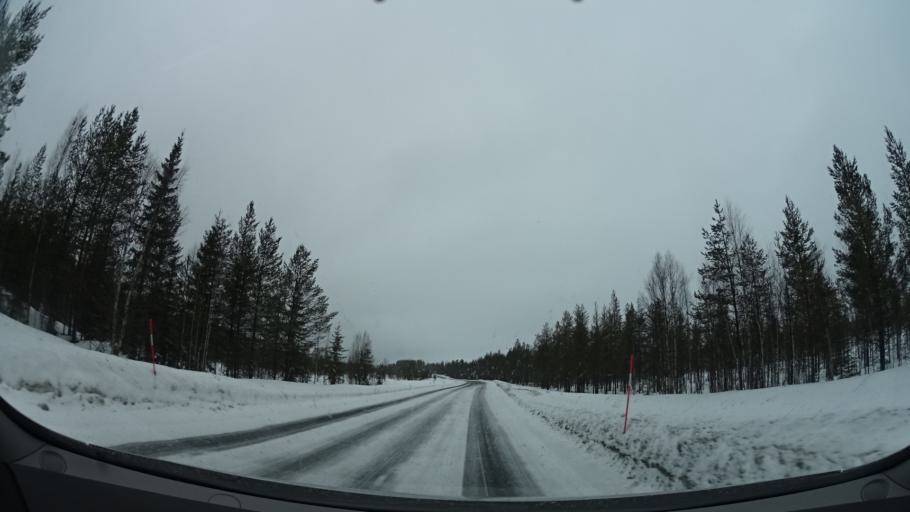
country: SE
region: Vaesterbotten
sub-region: Mala Kommun
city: Mala
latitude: 65.1381
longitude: 18.8544
